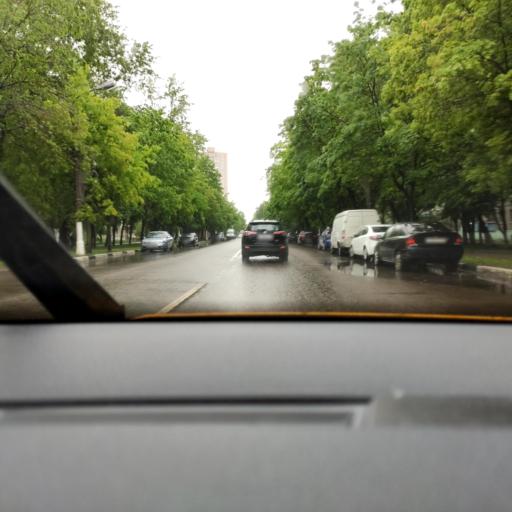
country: RU
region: Moskovskaya
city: Balashikha
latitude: 55.7958
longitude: 37.9693
